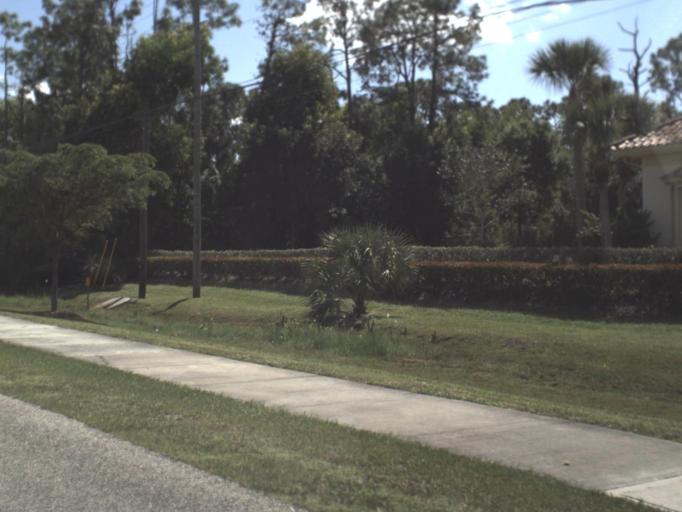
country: US
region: Florida
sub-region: Collier County
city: Lely Resort
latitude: 26.0683
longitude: -81.7072
